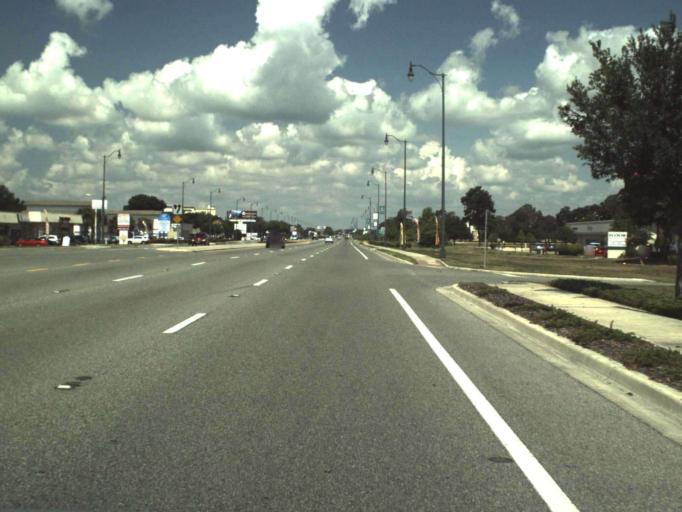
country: US
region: Florida
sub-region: Lake County
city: Silver Lake
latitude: 28.8244
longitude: -81.7908
